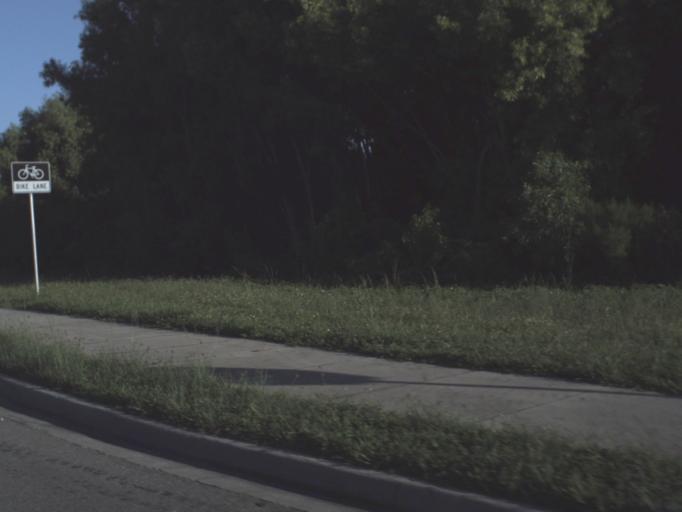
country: US
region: Florida
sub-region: Lee County
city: San Carlos Park
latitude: 26.4924
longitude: -81.8459
